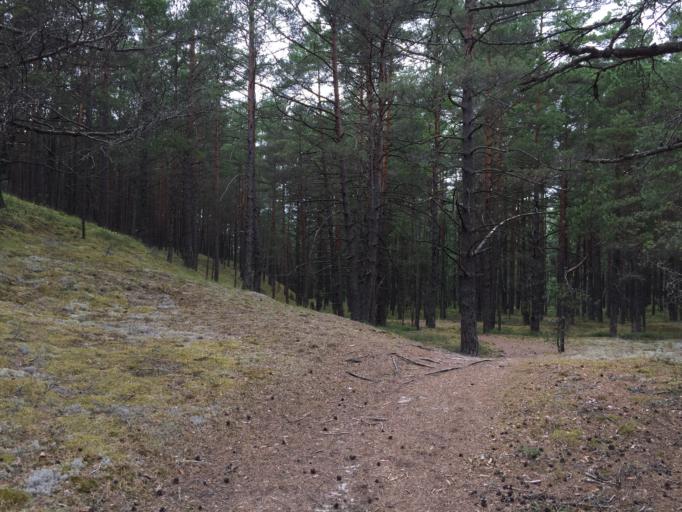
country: LV
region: Riga
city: Jaunciems
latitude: 57.1041
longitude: 24.1781
